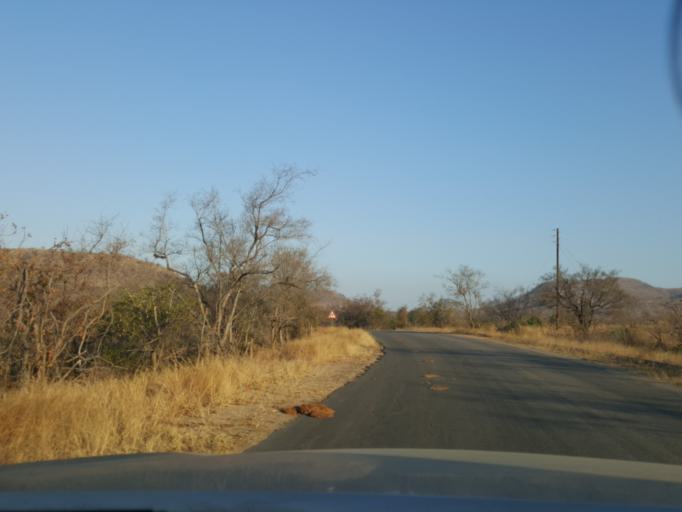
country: SZ
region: Hhohho
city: Ntfonjeni
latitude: -25.4357
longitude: 31.4439
